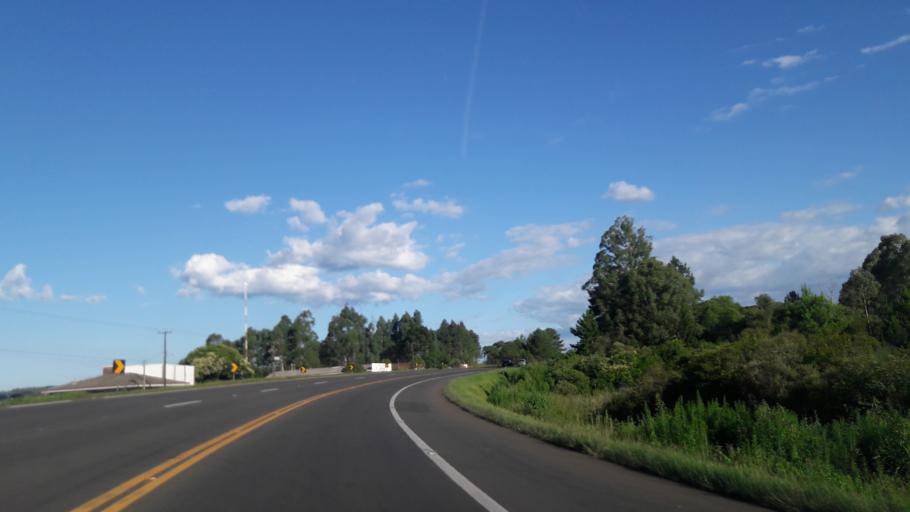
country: BR
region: Parana
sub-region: Guarapuava
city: Guarapuava
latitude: -25.3525
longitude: -51.3663
